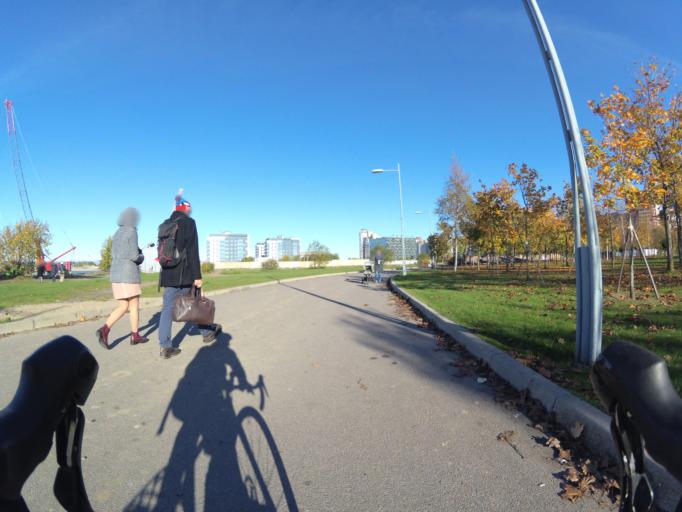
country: RU
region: Leningrad
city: Untolovo
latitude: 59.9848
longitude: 30.1886
